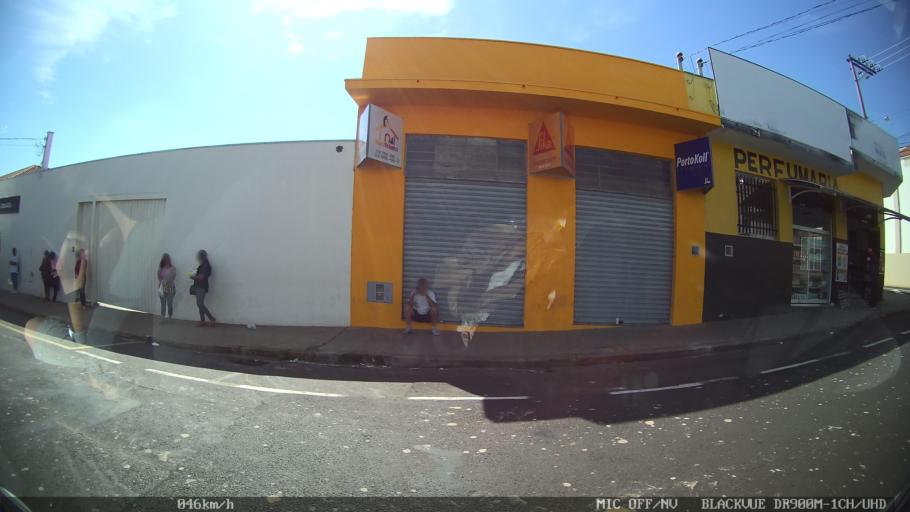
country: BR
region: Sao Paulo
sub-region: Franca
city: Franca
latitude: -20.5355
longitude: -47.4057
